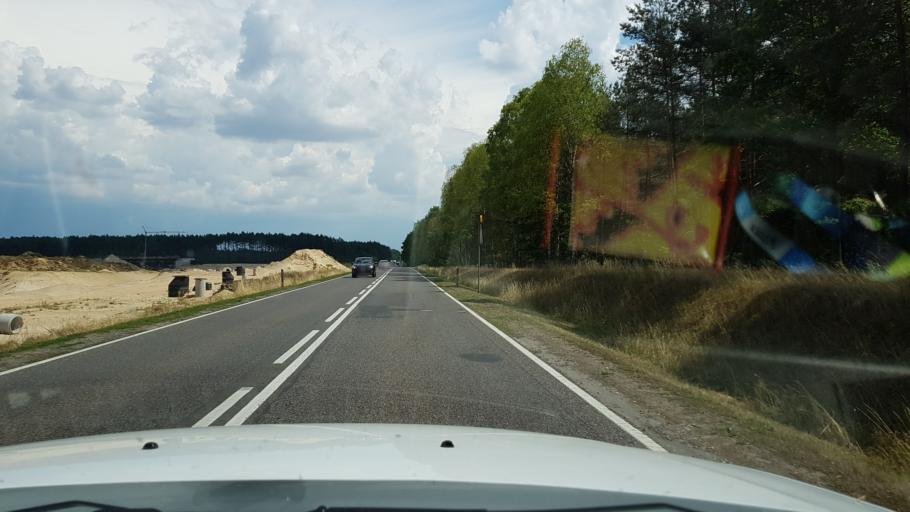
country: PL
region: West Pomeranian Voivodeship
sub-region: Powiat walecki
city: Walcz
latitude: 53.2978
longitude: 16.4191
